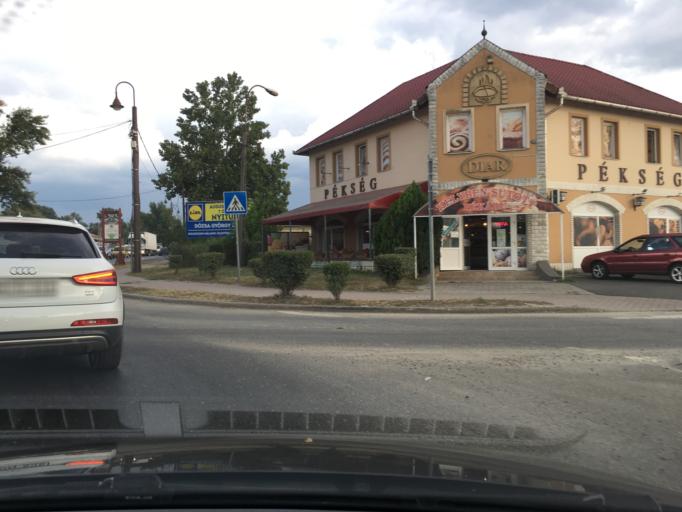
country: HU
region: Pest
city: Veresegyhaz
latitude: 47.6459
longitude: 19.2952
